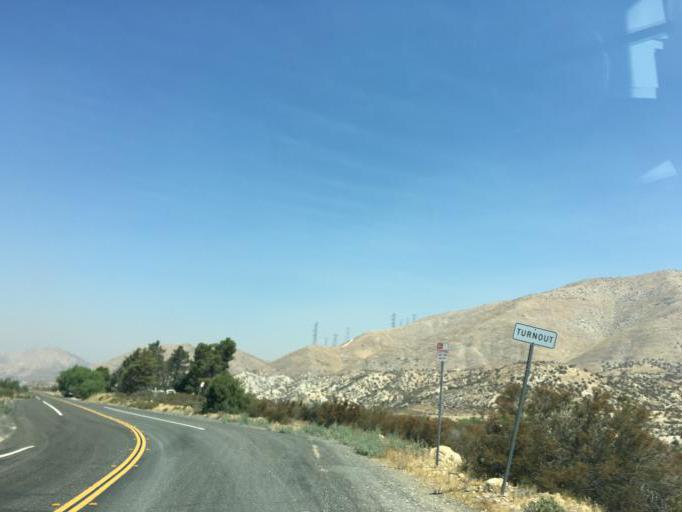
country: US
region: California
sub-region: Los Angeles County
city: Vincent
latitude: 34.4321
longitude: -118.1244
